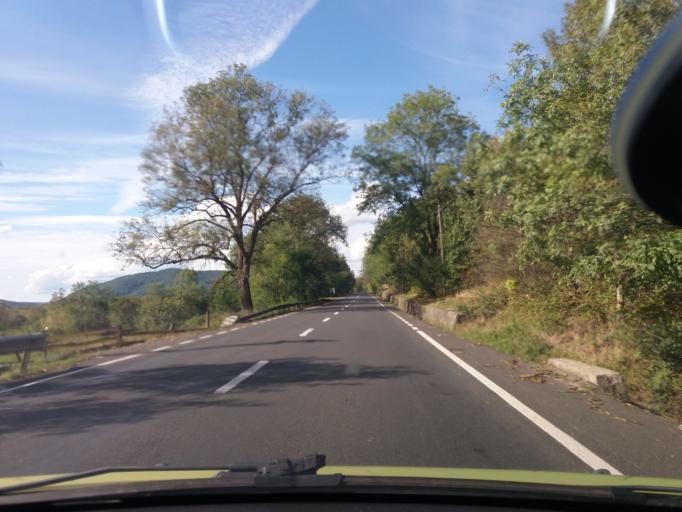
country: RO
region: Hunedoara
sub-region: Comuna Burjuc
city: Burjuc
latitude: 45.9546
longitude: 22.4852
